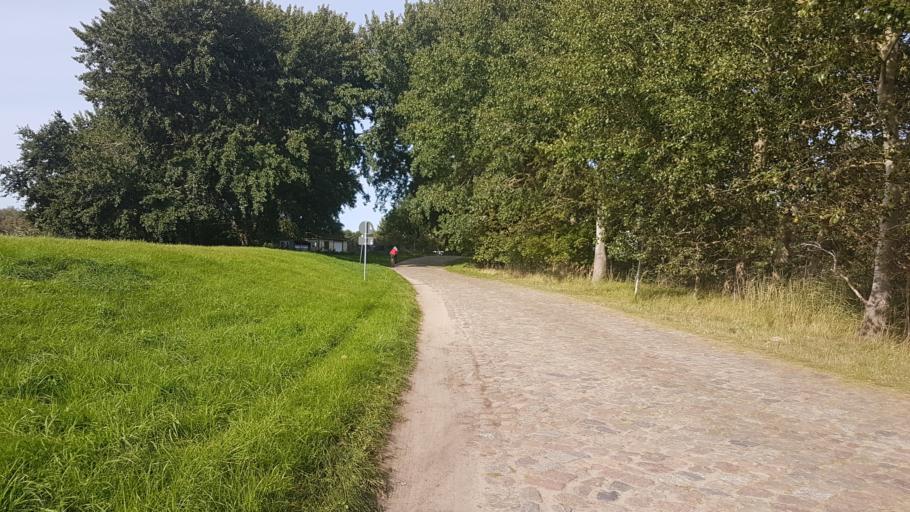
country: DE
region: Mecklenburg-Vorpommern
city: Gingst
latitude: 54.4304
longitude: 13.2061
